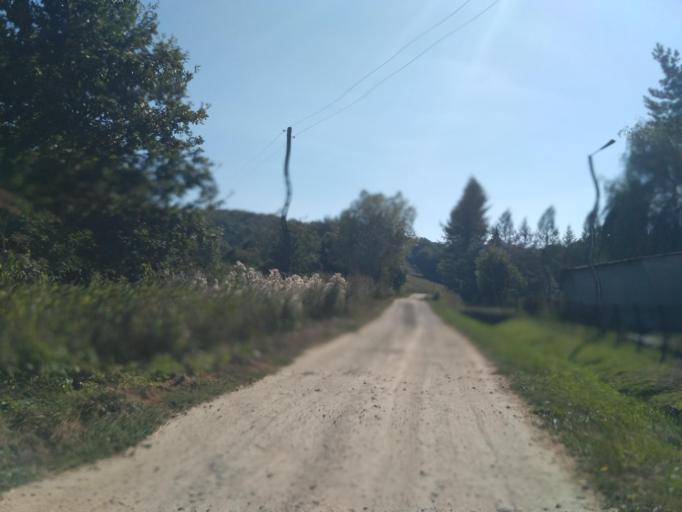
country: PL
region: Subcarpathian Voivodeship
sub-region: Powiat brzozowski
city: Humniska
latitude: 49.7045
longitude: 22.0519
